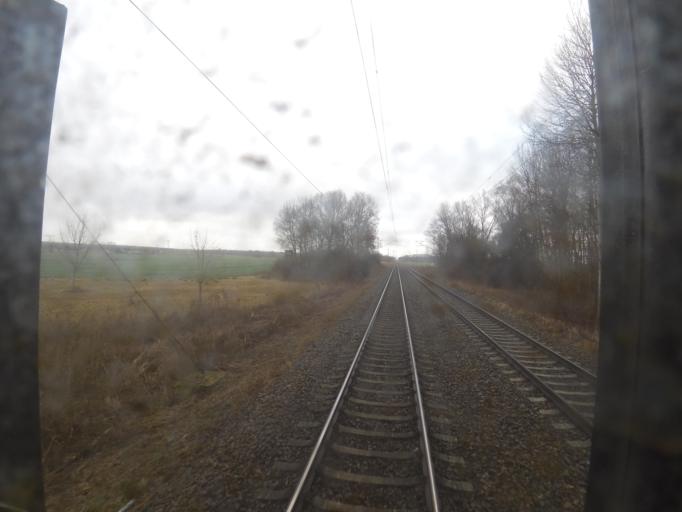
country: DE
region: Brandenburg
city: Zossen
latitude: 52.2049
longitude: 13.4422
